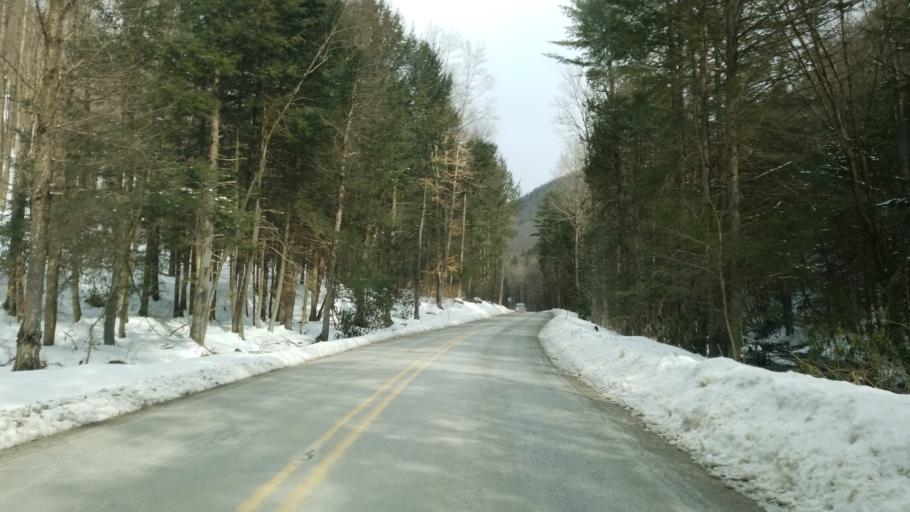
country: US
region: Pennsylvania
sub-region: Clearfield County
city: Shiloh
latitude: 41.2561
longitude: -78.1520
